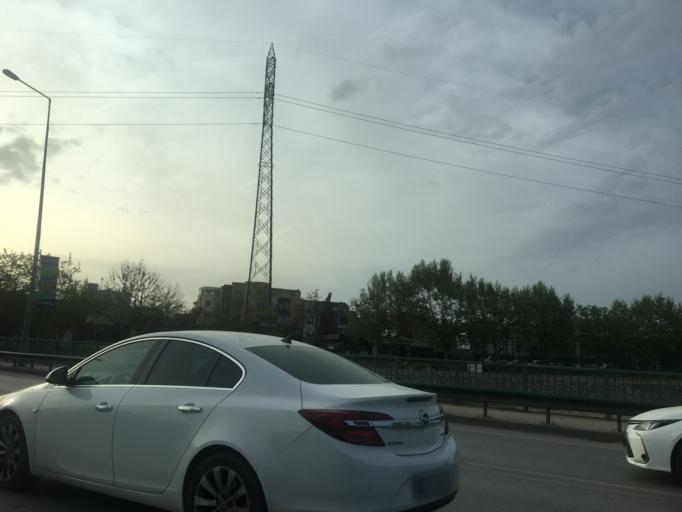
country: TR
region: Bursa
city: Yildirim
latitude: 40.2133
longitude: 29.0097
